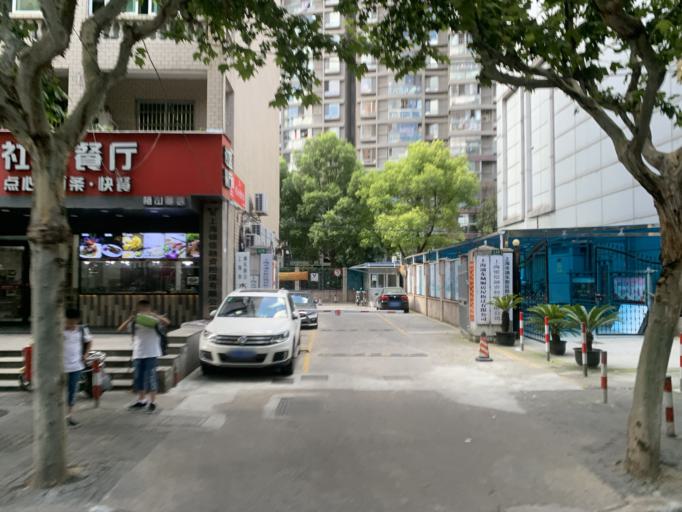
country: CN
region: Shanghai Shi
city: Pudong
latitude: 31.2454
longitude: 121.5406
